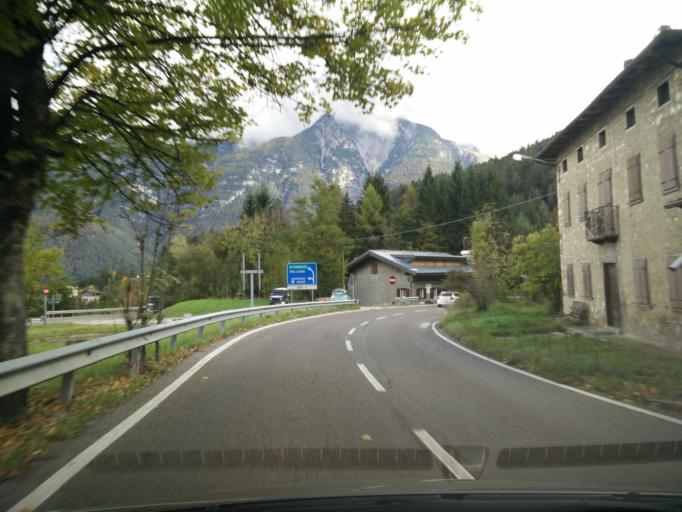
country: IT
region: Veneto
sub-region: Provincia di Belluno
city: Pieve di Cadore
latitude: 46.4219
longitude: 12.3662
